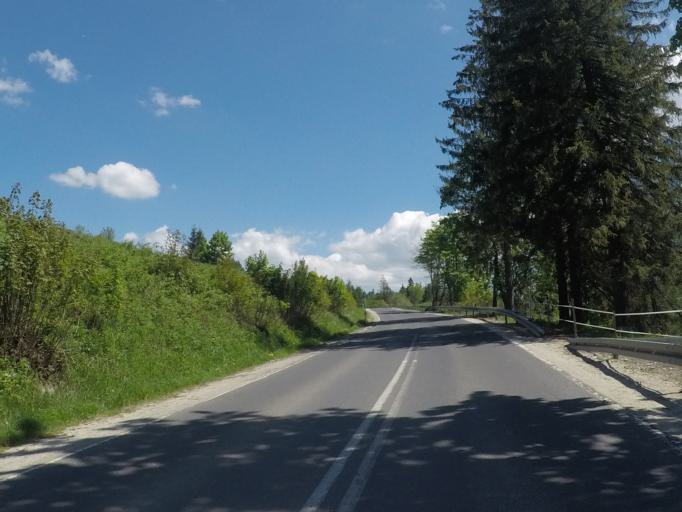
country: PL
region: Lesser Poland Voivodeship
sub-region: Powiat tatrzanski
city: Bukowina Tatrzanska
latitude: 49.3317
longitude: 20.0845
